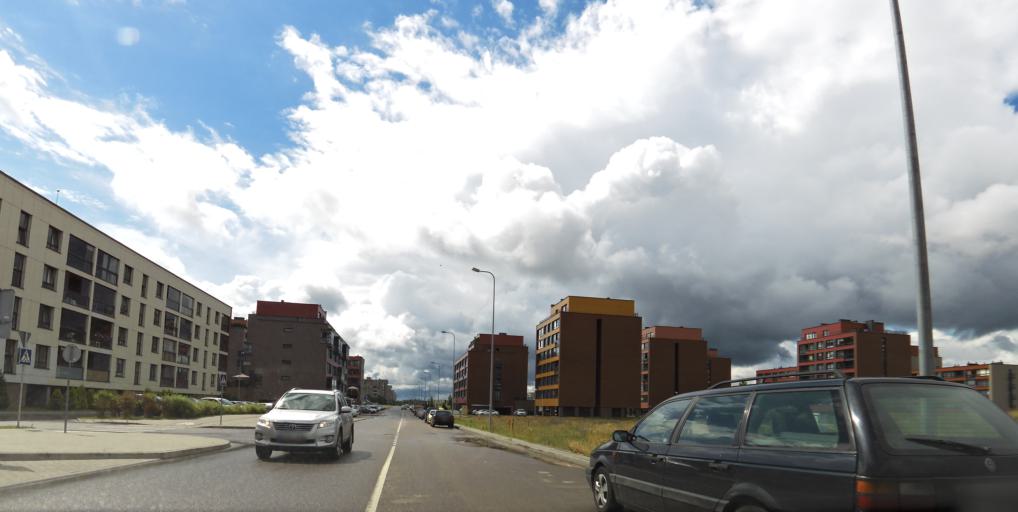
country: LT
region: Vilnius County
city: Pilaite
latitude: 54.7134
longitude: 25.1821
